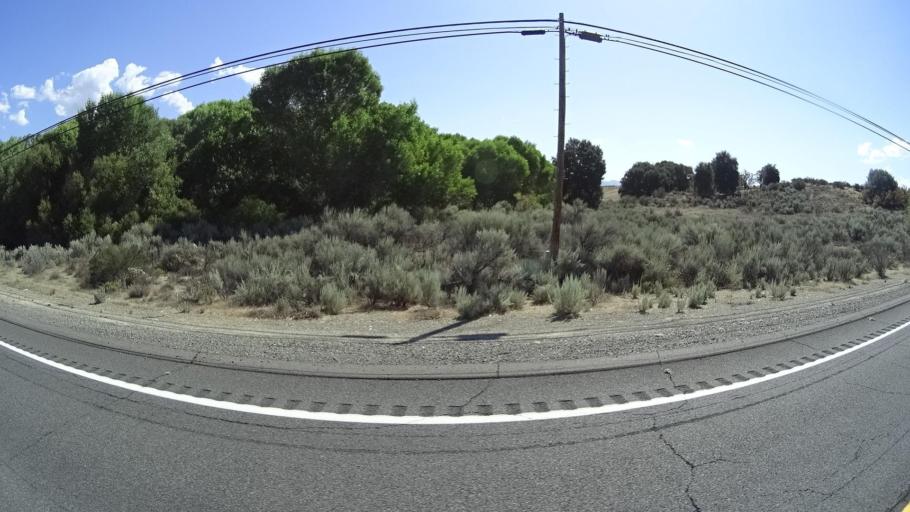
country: US
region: California
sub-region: Riverside County
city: Aguanga
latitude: 33.3088
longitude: -116.6928
